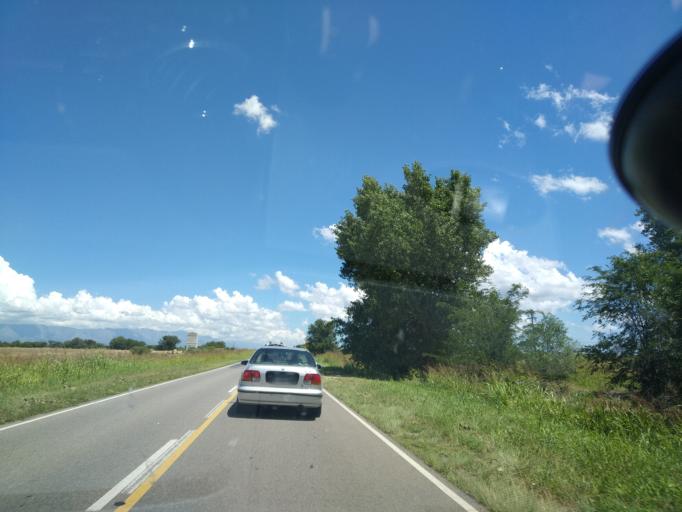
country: AR
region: Cordoba
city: Villa Cura Brochero
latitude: -31.6197
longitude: -65.1094
